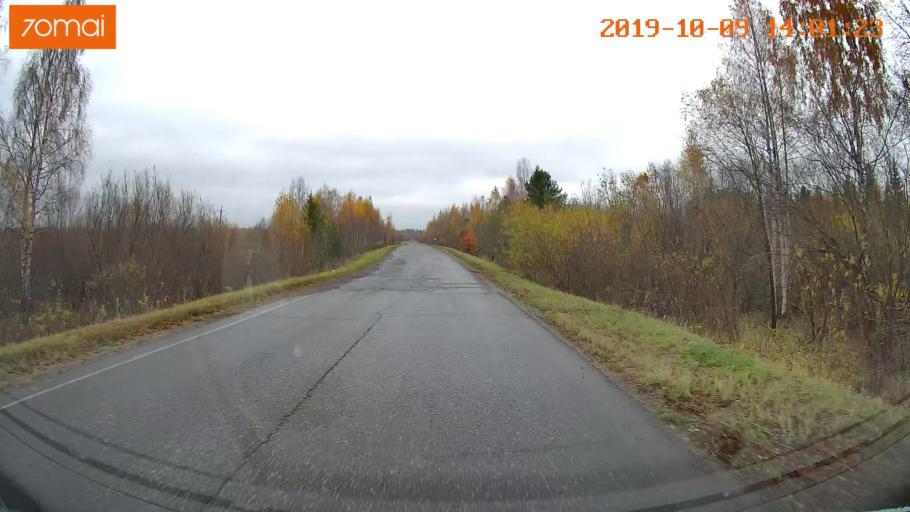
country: RU
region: Kostroma
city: Buy
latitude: 58.4433
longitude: 41.3472
